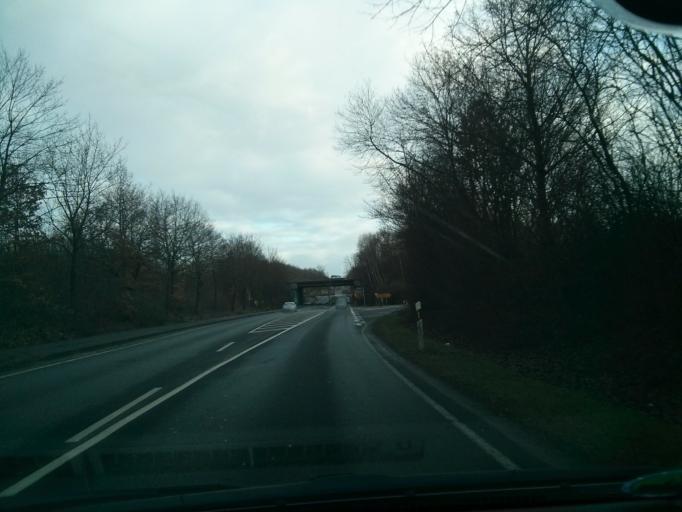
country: DE
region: North Rhine-Westphalia
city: Meckenheim
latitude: 50.6410
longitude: 7.0340
